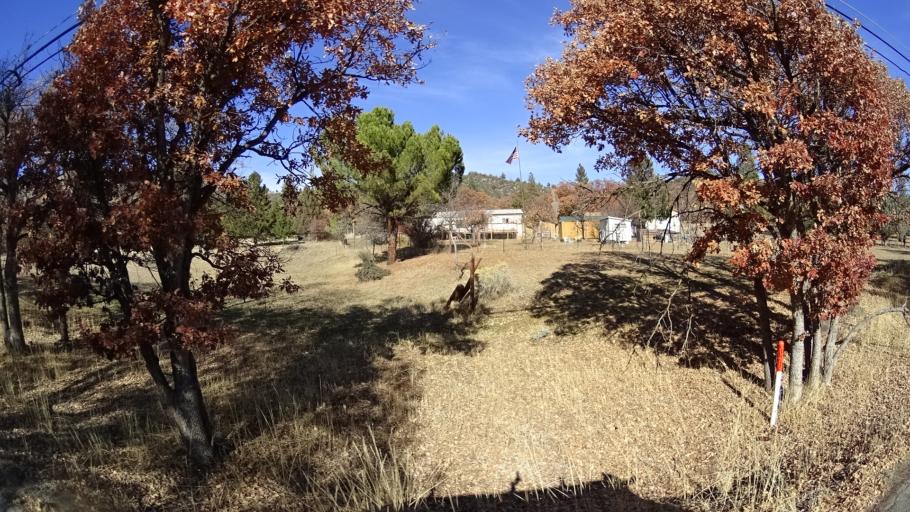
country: US
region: California
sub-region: Siskiyou County
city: Yreka
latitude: 41.7151
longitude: -122.6593
